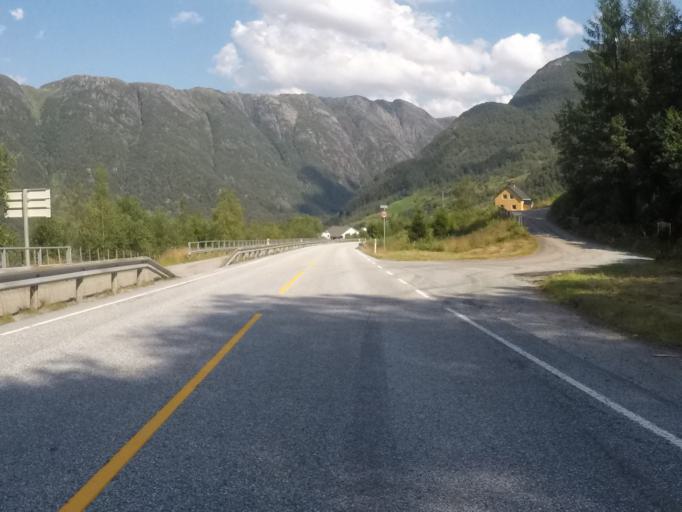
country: NO
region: Hordaland
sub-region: Masfjorden
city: Masfjorden
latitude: 60.8993
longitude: 5.5215
